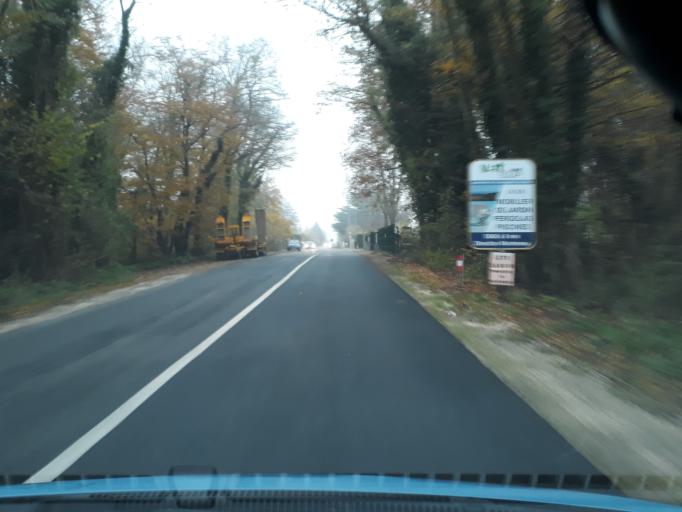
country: FR
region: Ile-de-France
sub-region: Departement de Seine-et-Marne
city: Veneux-les-Sablons
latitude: 48.3870
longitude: 2.7790
